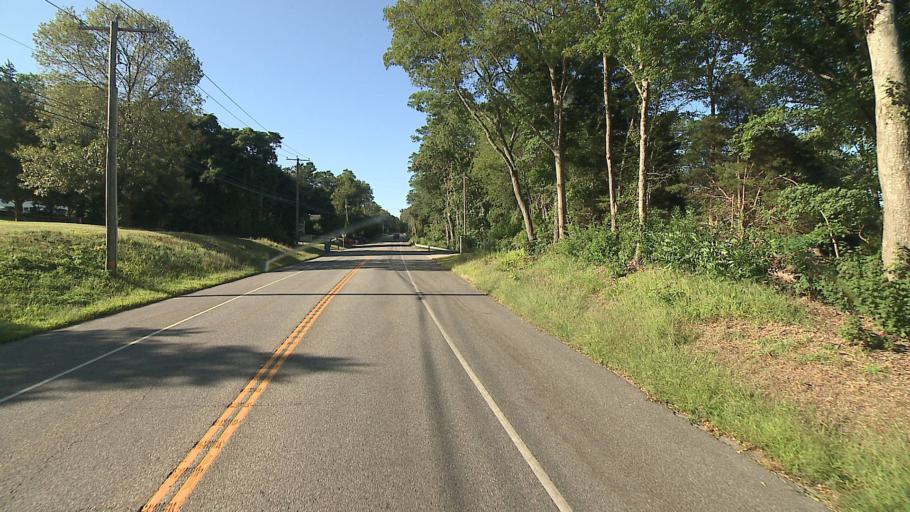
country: US
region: Connecticut
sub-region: New London County
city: Gales Ferry
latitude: 41.4675
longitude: -72.0588
